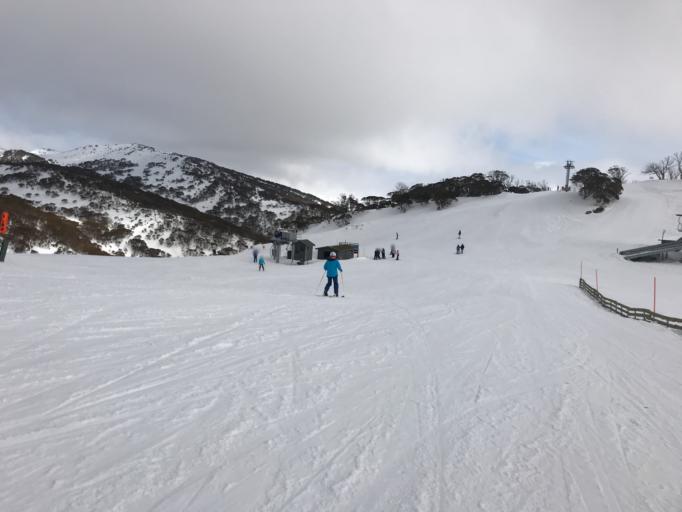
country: AU
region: New South Wales
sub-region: Snowy River
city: Jindabyne
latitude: -36.3824
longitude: 148.3800
